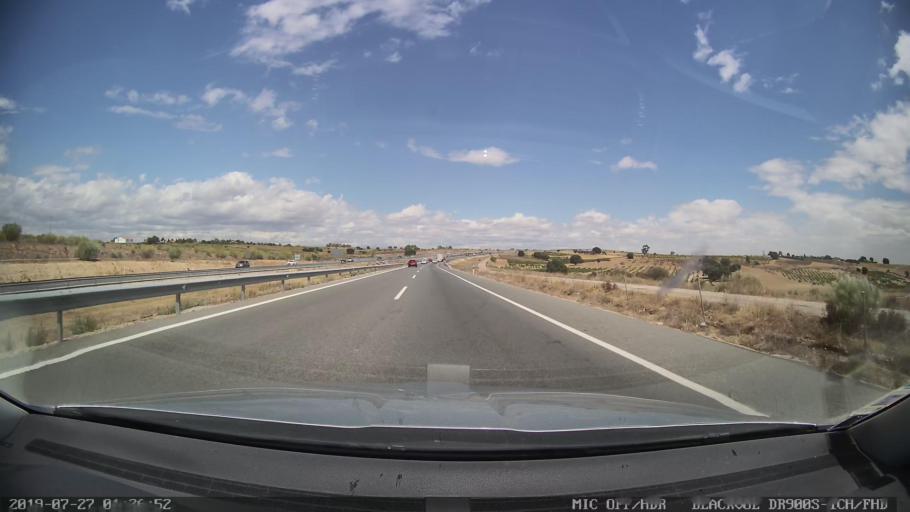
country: ES
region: Castille-La Mancha
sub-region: Province of Toledo
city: La Torre de Esteban Hambran
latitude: 40.1643
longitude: -4.1684
